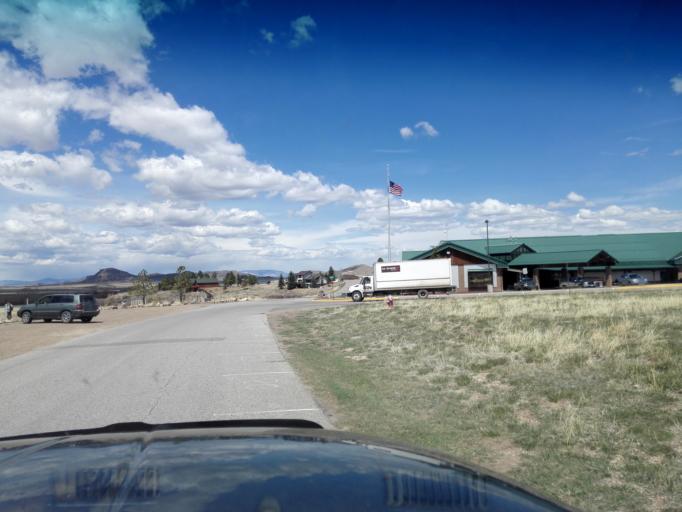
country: US
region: Colorado
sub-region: Custer County
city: Westcliffe
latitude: 38.1358
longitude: -105.4722
